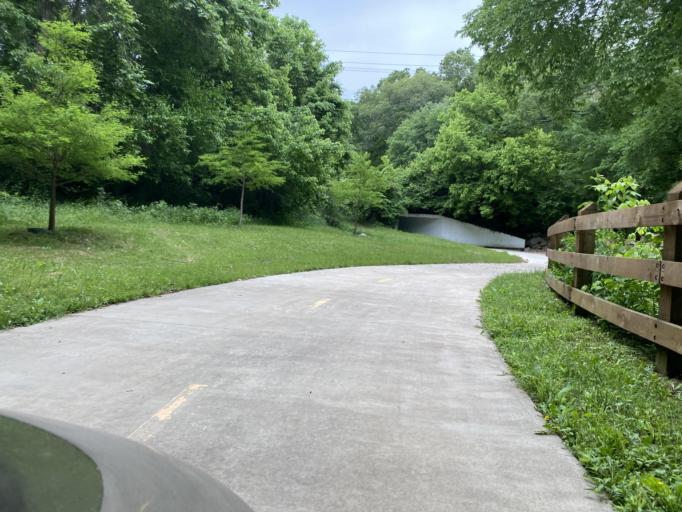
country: US
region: Arkansas
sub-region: Benton County
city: Bentonville
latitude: 36.3731
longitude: -94.2382
